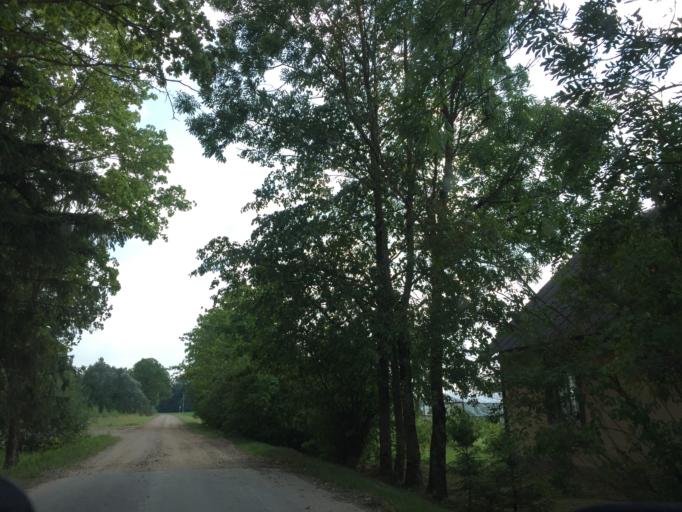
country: LV
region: Jelgava
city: Jelgava
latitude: 56.5104
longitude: 23.7548
